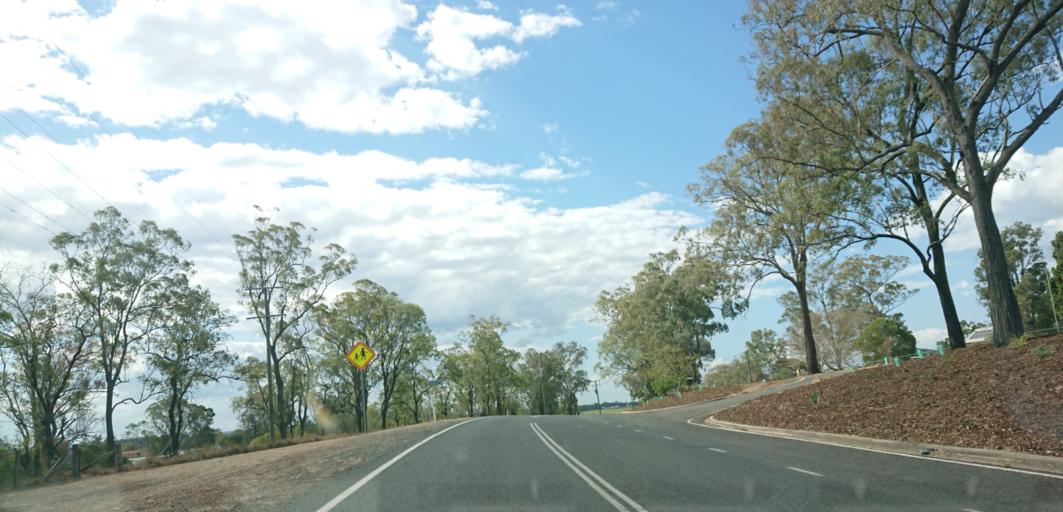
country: AU
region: Queensland
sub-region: Lockyer Valley
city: Gatton
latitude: -27.6298
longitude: 152.1887
